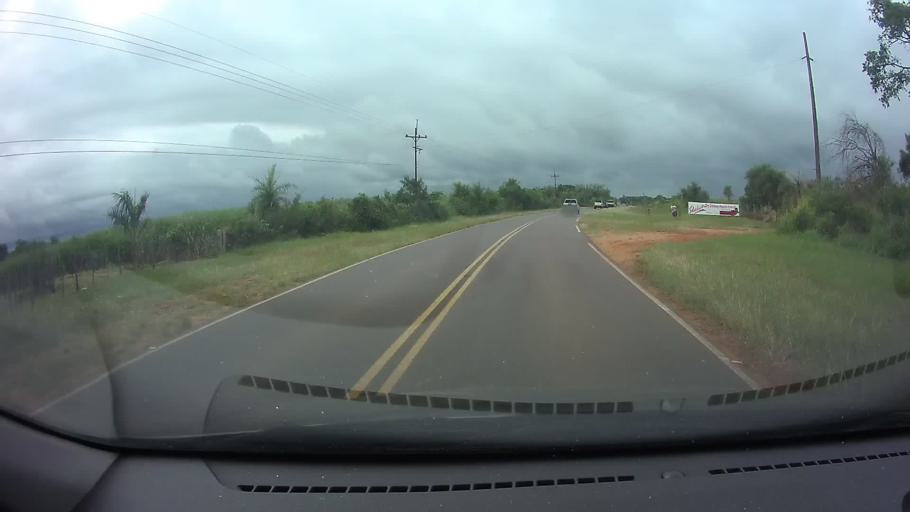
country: PY
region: Central
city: Nueva Italia
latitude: -25.6005
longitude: -57.4926
